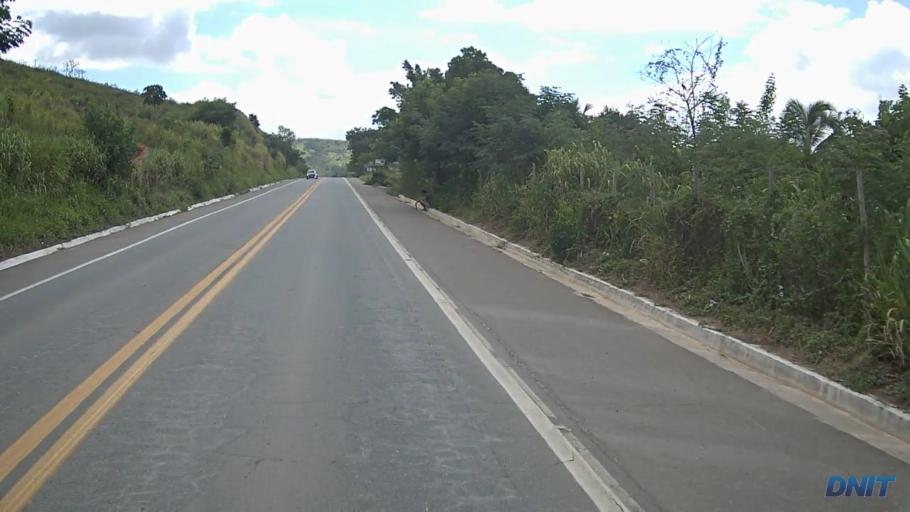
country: BR
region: Minas Gerais
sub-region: Governador Valadares
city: Governador Valadares
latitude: -18.9283
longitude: -42.0420
